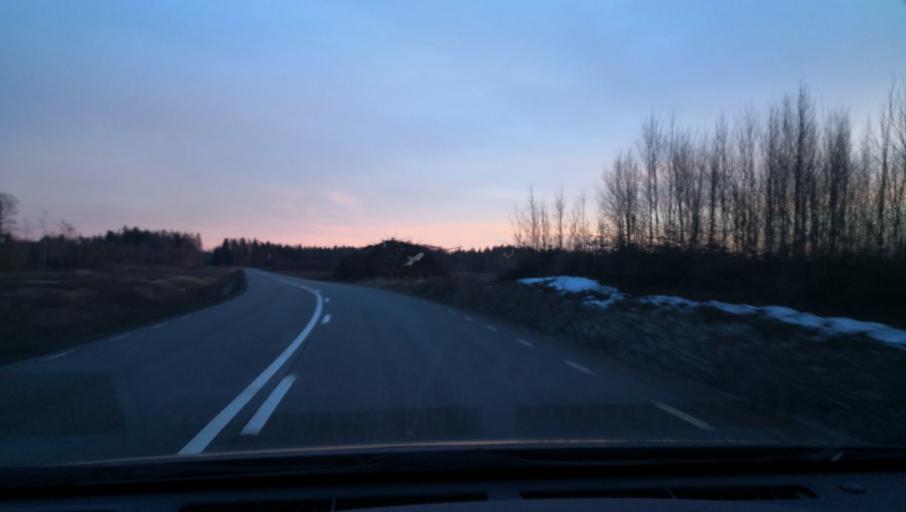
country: SE
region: OErebro
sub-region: Orebro Kommun
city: Orebro
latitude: 59.2377
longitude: 15.1073
